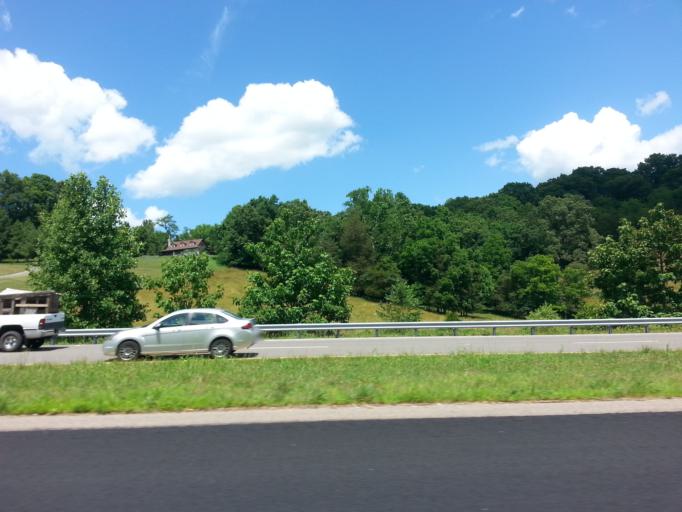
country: US
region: Virginia
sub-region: Lee County
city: Jonesville
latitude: 36.6770
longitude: -83.2140
